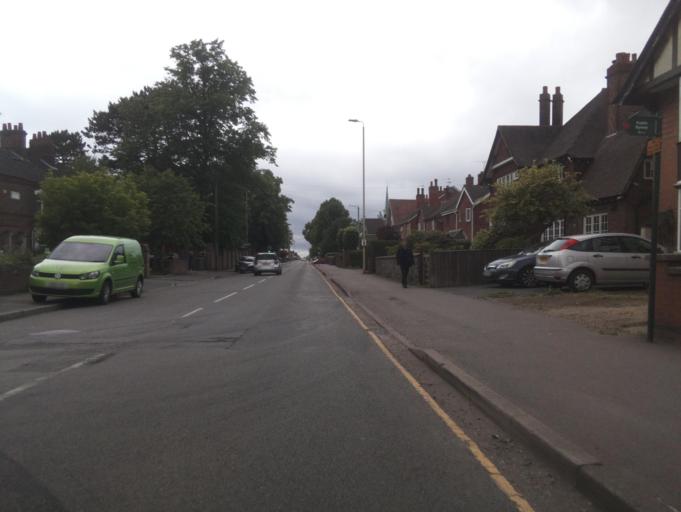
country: GB
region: England
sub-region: Leicestershire
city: Coalville
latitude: 52.7221
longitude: -1.3638
